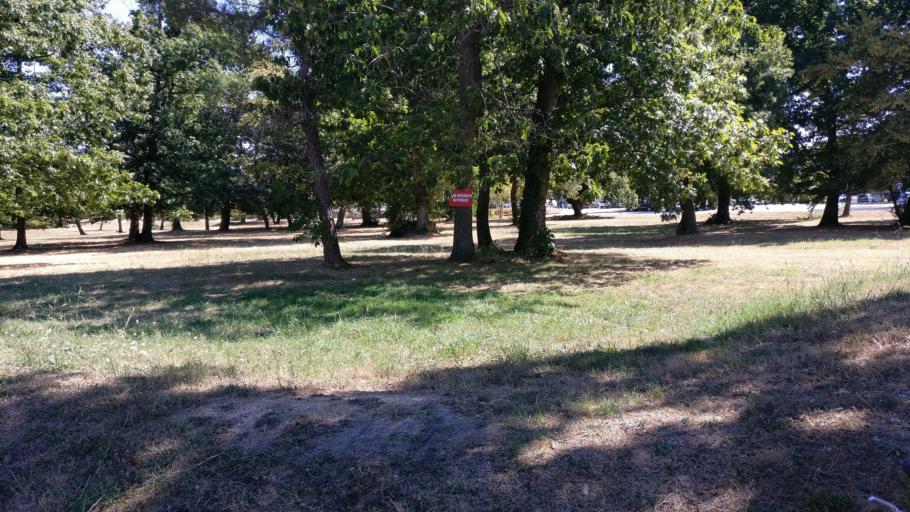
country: FR
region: Aquitaine
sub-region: Departement de la Gironde
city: Talence
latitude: 44.7992
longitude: -0.6190
